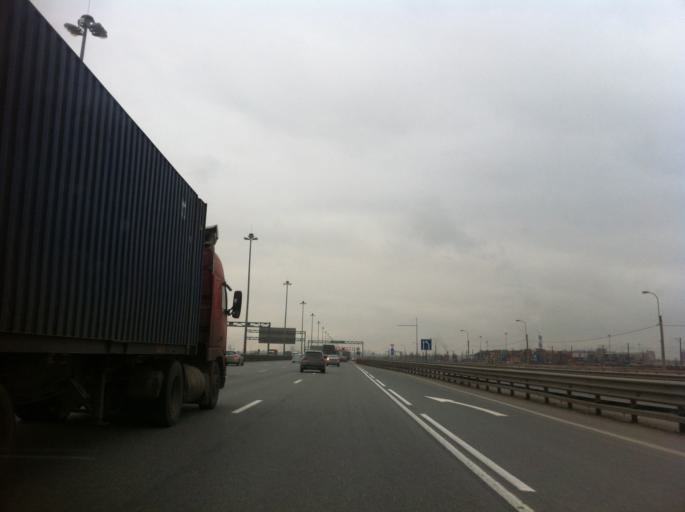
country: RU
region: St.-Petersburg
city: Kupchino
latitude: 59.8145
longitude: 30.3160
